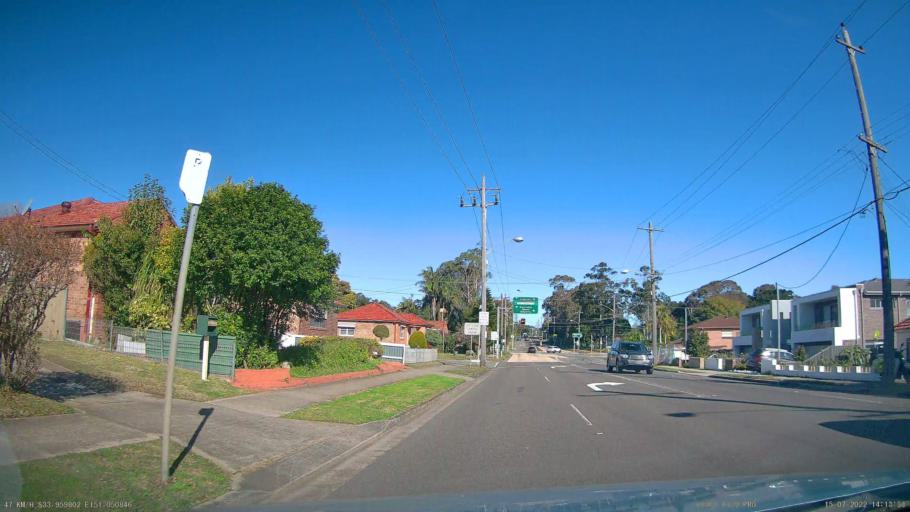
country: AU
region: New South Wales
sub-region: Hurstville
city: Peakhurst
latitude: -33.9600
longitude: 151.0508
